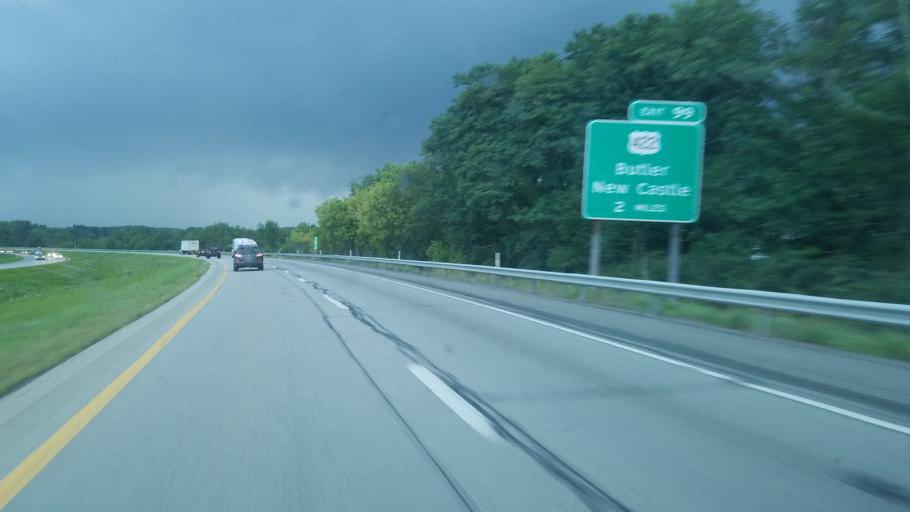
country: US
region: Pennsylvania
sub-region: Butler County
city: Slippery Rock
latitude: 40.9911
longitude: -80.1289
